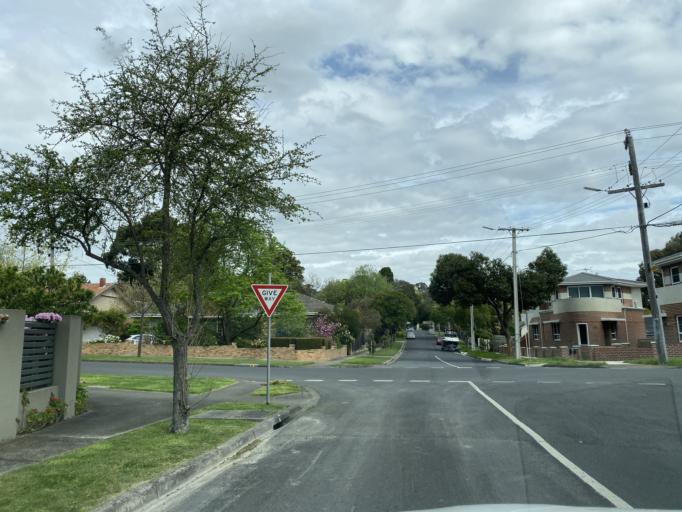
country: AU
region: Victoria
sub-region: Whitehorse
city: Surrey Hills
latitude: -37.8339
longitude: 145.1063
